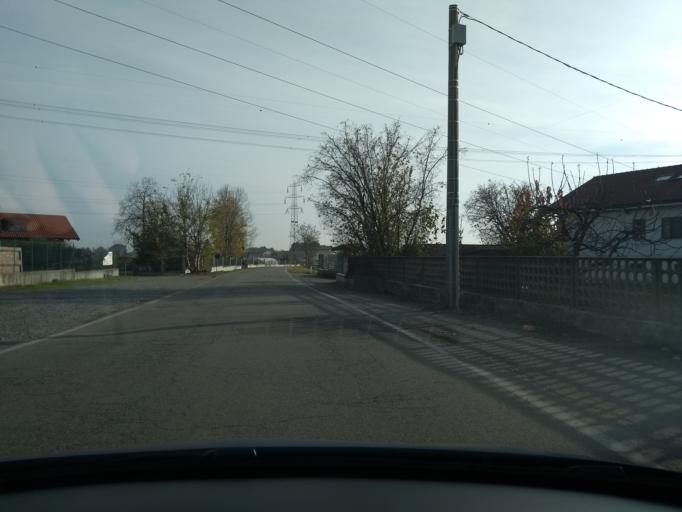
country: IT
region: Piedmont
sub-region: Provincia di Torino
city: Mathi
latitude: 45.2652
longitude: 7.5325
